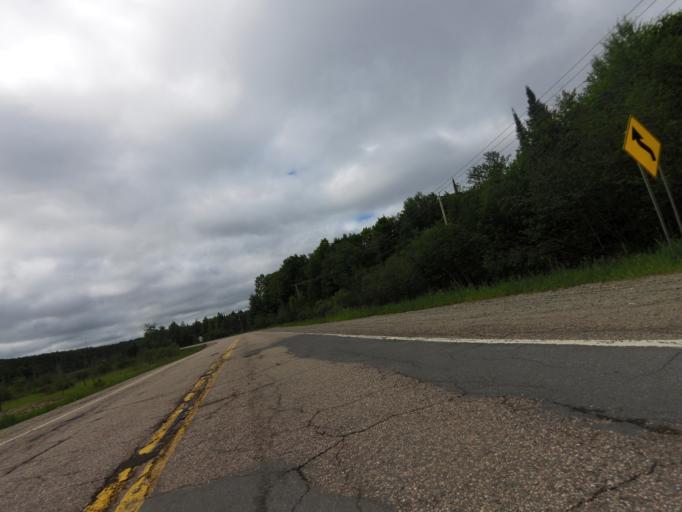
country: CA
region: Quebec
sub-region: Outaouais
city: Shawville
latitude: 45.8178
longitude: -76.4605
